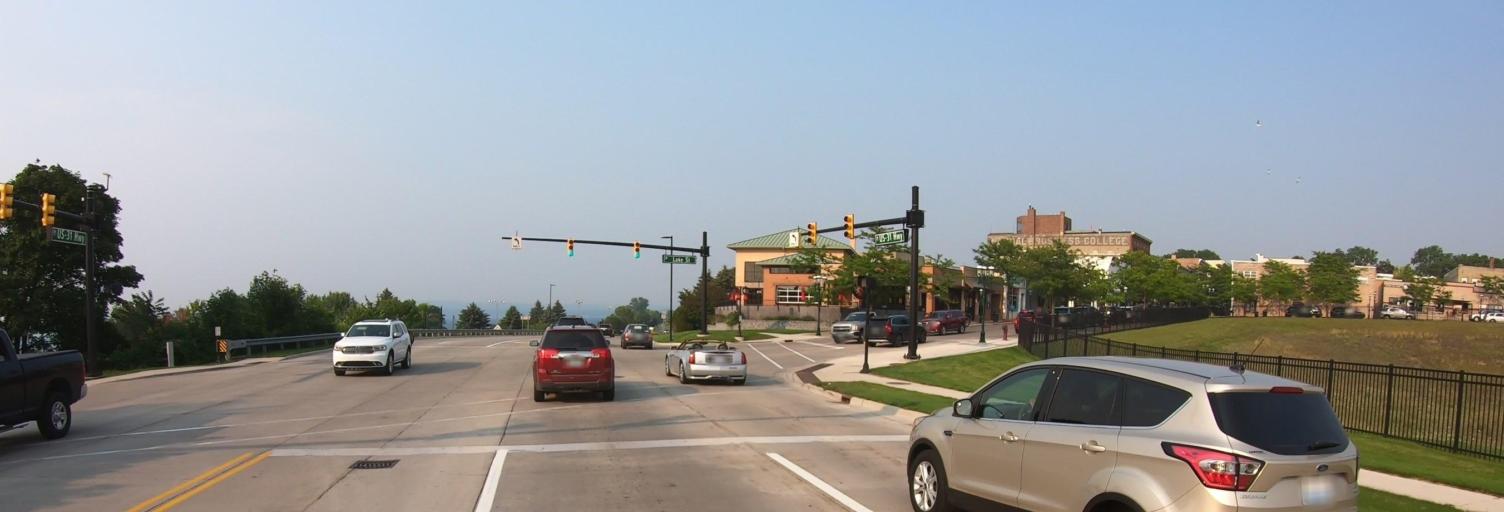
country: US
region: Michigan
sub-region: Emmet County
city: Petoskey
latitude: 45.3749
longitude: -84.9600
